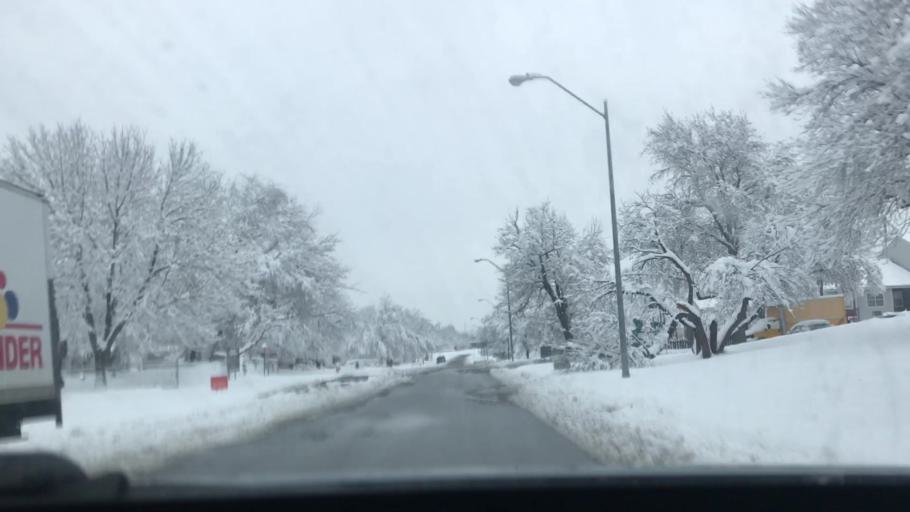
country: US
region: Missouri
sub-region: Jackson County
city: Grandview
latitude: 38.9177
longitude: -94.5301
